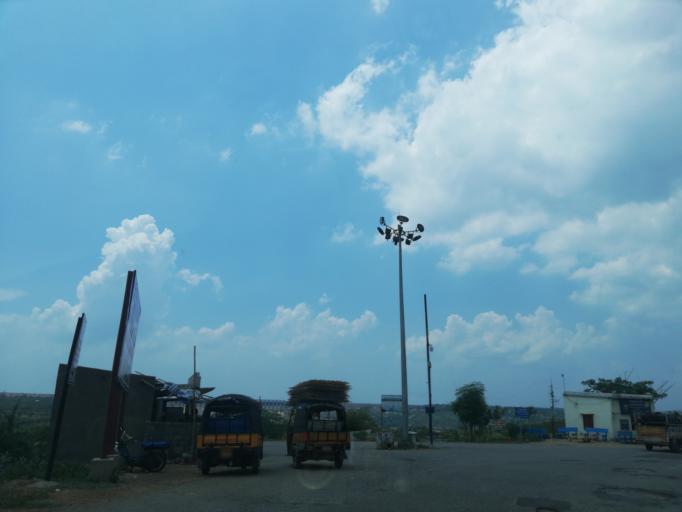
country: IN
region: Andhra Pradesh
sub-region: Guntur
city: Macherla
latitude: 16.5669
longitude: 79.3335
